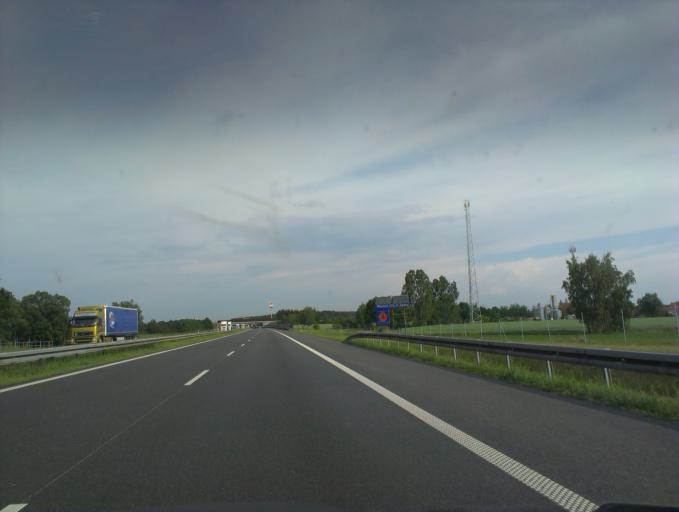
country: PL
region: Opole Voivodeship
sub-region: Powiat opolski
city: Niemodlin
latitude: 50.6825
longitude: 17.6434
